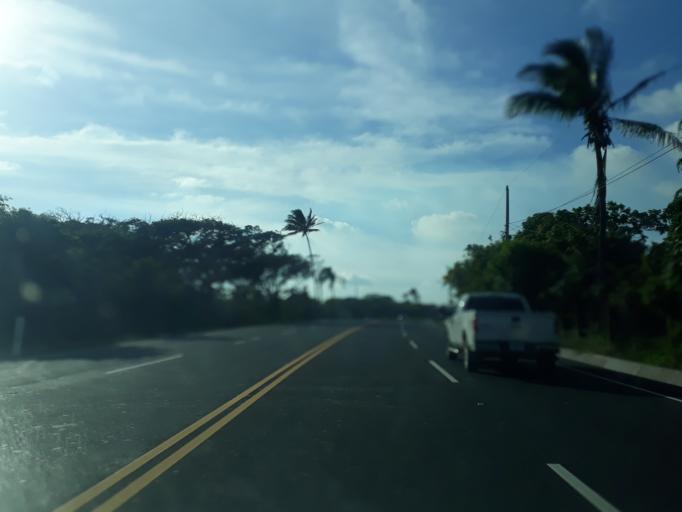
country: NI
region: Carazo
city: Diriamba
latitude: 11.9186
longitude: -86.2766
